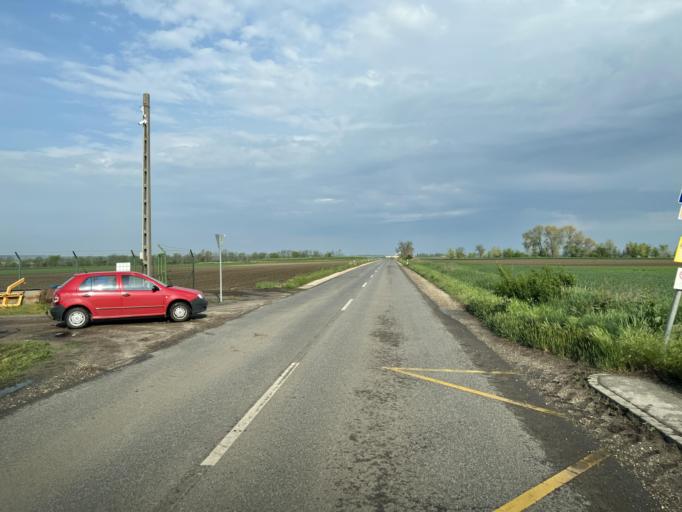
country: HU
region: Pest
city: Tapioszentmarton
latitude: 47.3178
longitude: 19.7510
